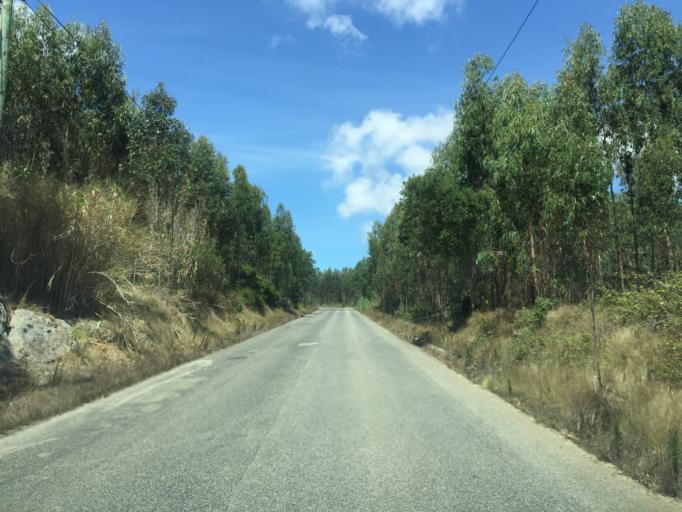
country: PT
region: Lisbon
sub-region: Lourinha
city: Lourinha
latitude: 39.2712
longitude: -9.2902
